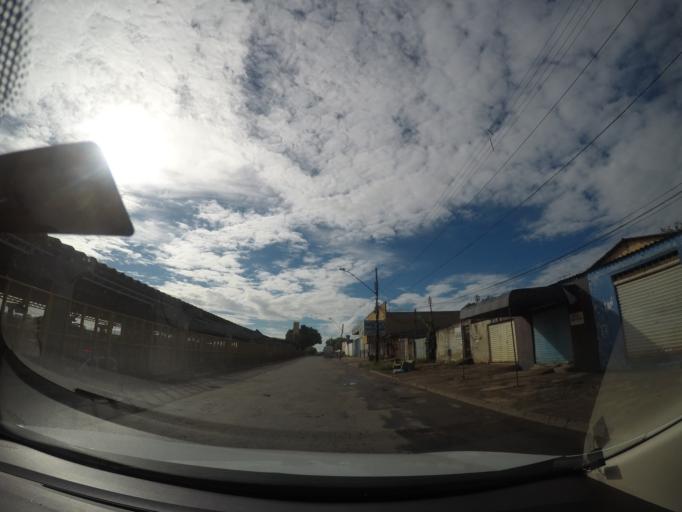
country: BR
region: Goias
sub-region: Goiania
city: Goiania
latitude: -16.6663
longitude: -49.2124
